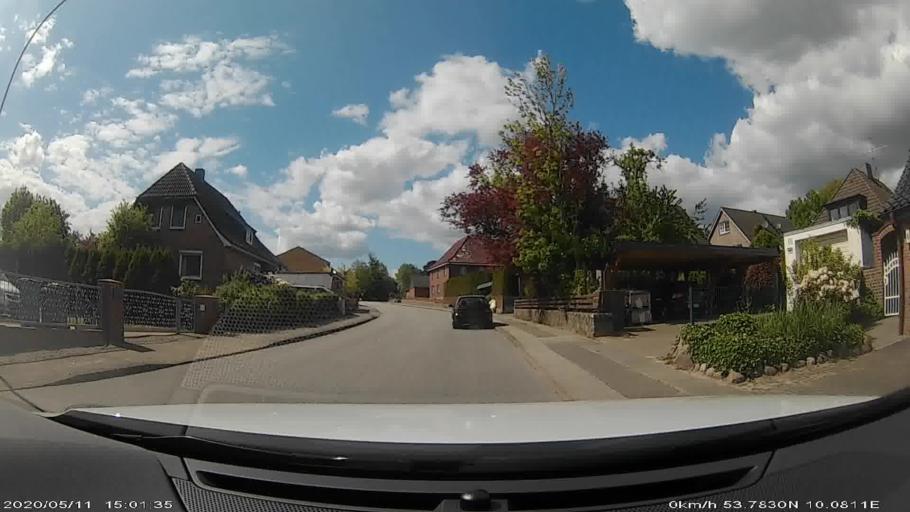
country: DE
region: Schleswig-Holstein
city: Huttblek
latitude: 53.7893
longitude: 10.0687
